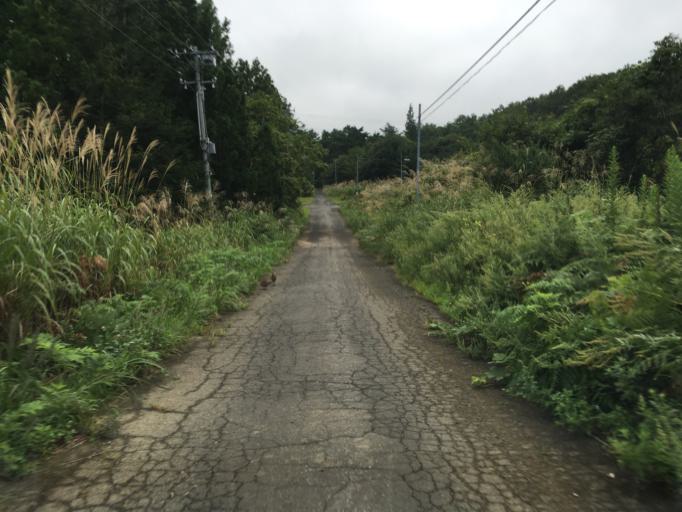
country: JP
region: Fukushima
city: Fukushima-shi
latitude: 37.8100
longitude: 140.3437
